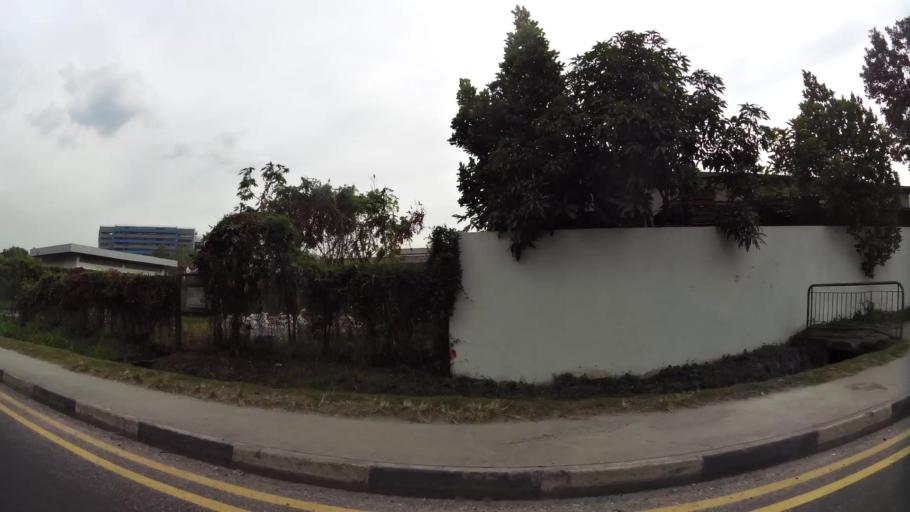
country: MY
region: Johor
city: Johor Bahru
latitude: 1.4342
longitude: 103.7518
